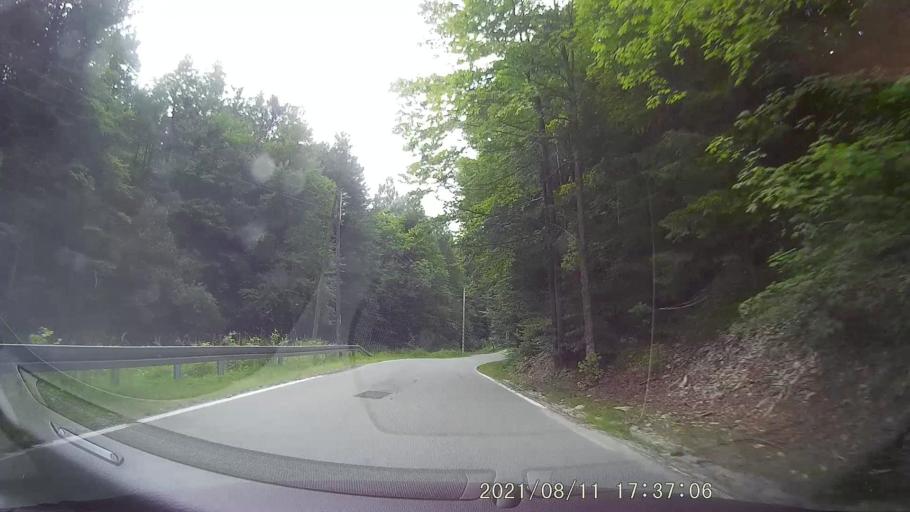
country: PL
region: Lower Silesian Voivodeship
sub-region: Powiat klodzki
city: Duszniki-Zdroj
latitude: 50.3357
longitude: 16.4052
